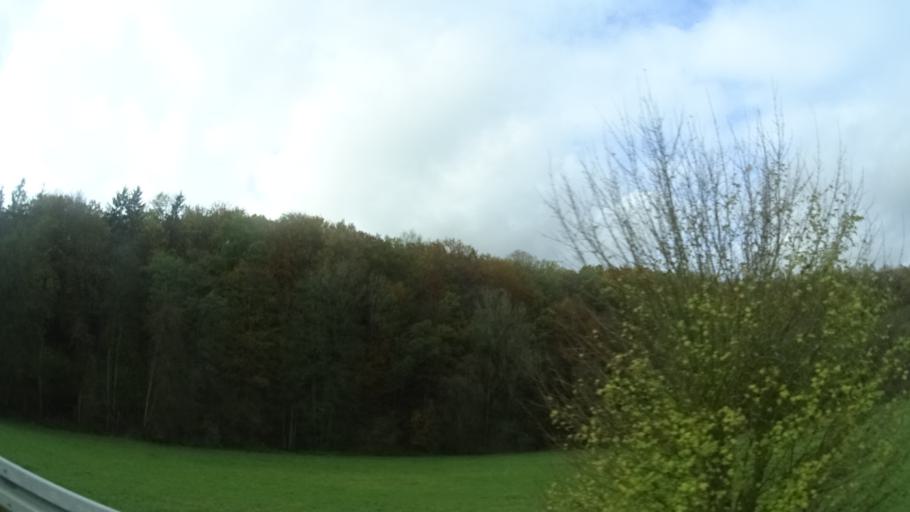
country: DE
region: Bavaria
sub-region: Regierungsbezirk Unterfranken
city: Aubstadt
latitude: 50.3416
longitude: 10.3999
